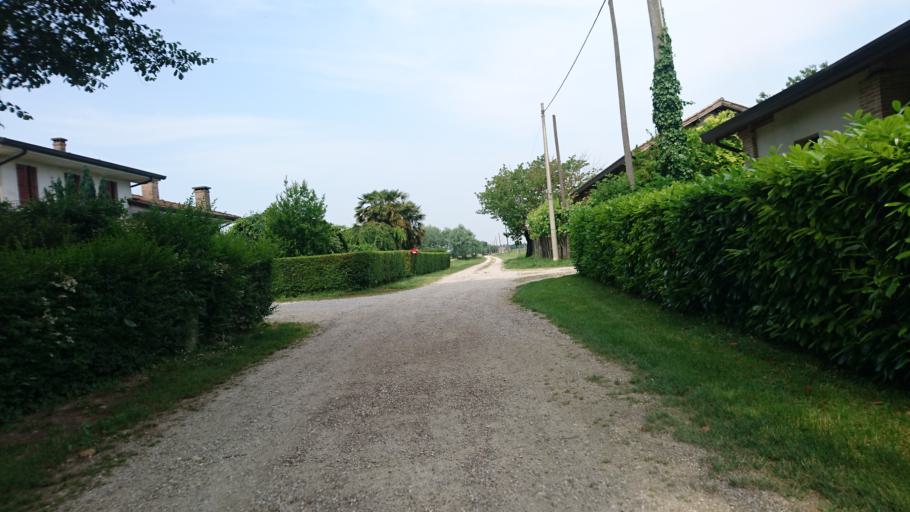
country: IT
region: Veneto
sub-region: Provincia di Padova
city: Polverara
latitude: 45.3249
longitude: 11.9549
